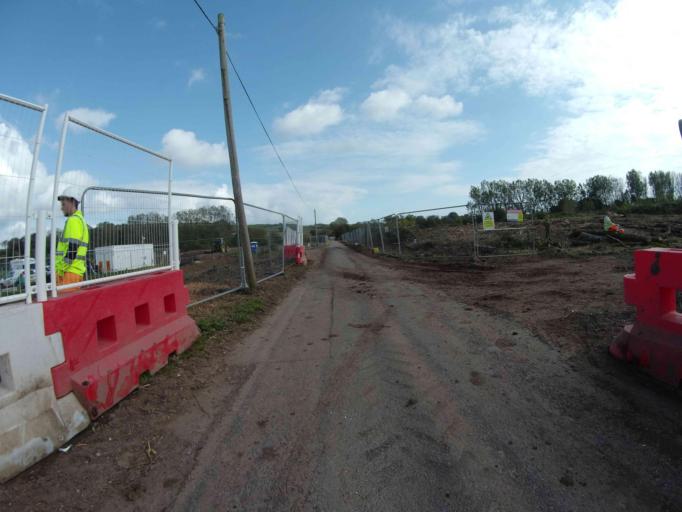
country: GB
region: England
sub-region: Devon
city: Budleigh Salterton
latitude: 50.6395
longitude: -3.3123
